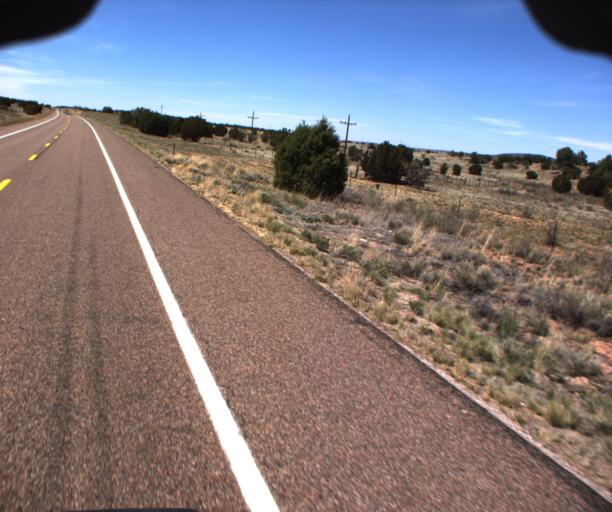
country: US
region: Arizona
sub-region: Mohave County
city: Peach Springs
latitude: 35.5127
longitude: -113.1916
